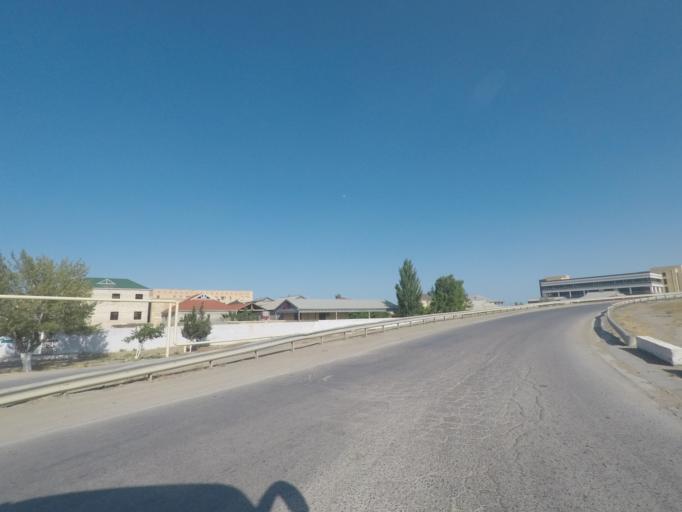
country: AZ
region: Baki
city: Qobustan
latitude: 40.0754
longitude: 49.4123
